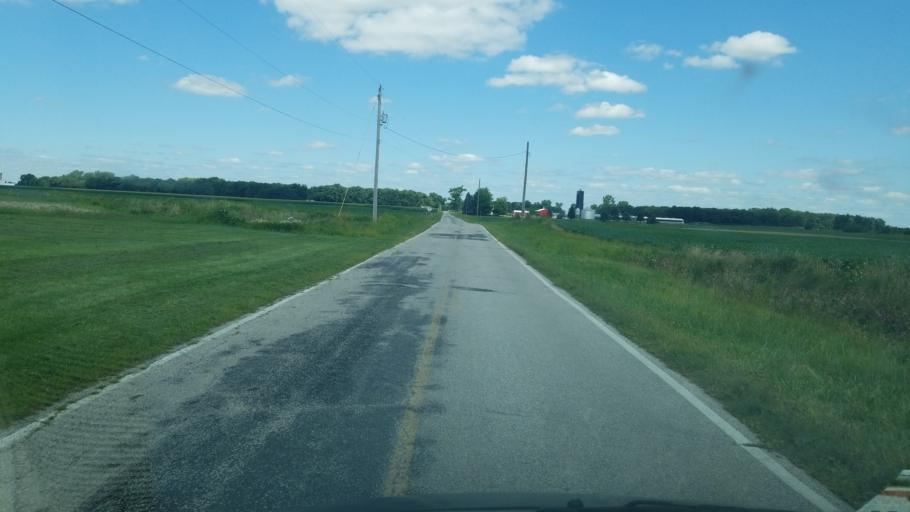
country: US
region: Ohio
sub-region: Fulton County
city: Delta
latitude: 41.6182
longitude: -84.0147
